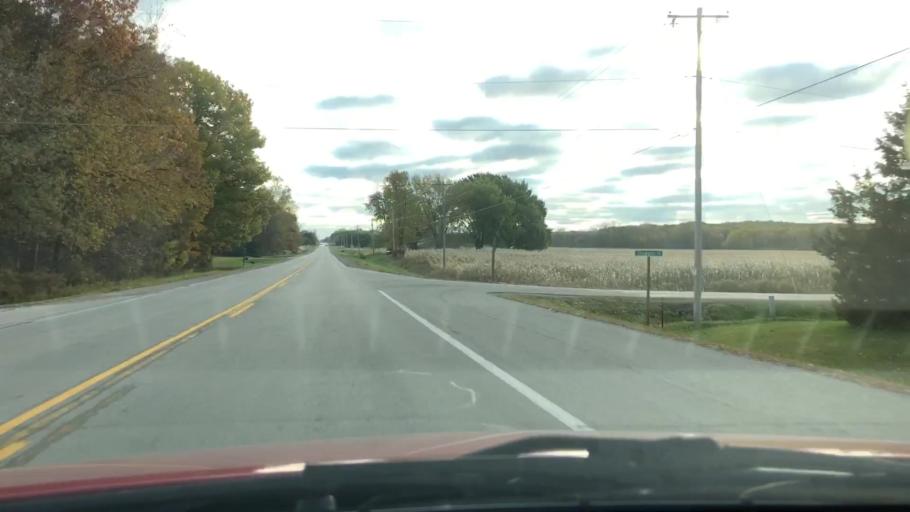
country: US
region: Wisconsin
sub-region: Brown County
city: Oneida
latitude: 44.4443
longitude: -88.2211
